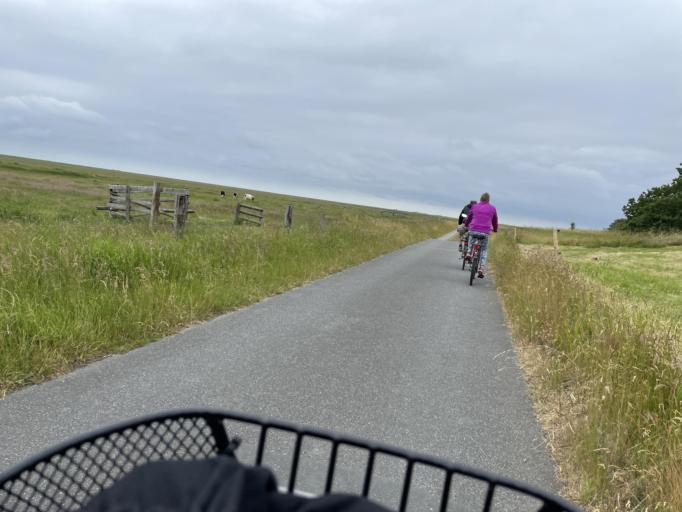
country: DE
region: Lower Saxony
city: Nordholz
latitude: 53.8220
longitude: 8.5790
